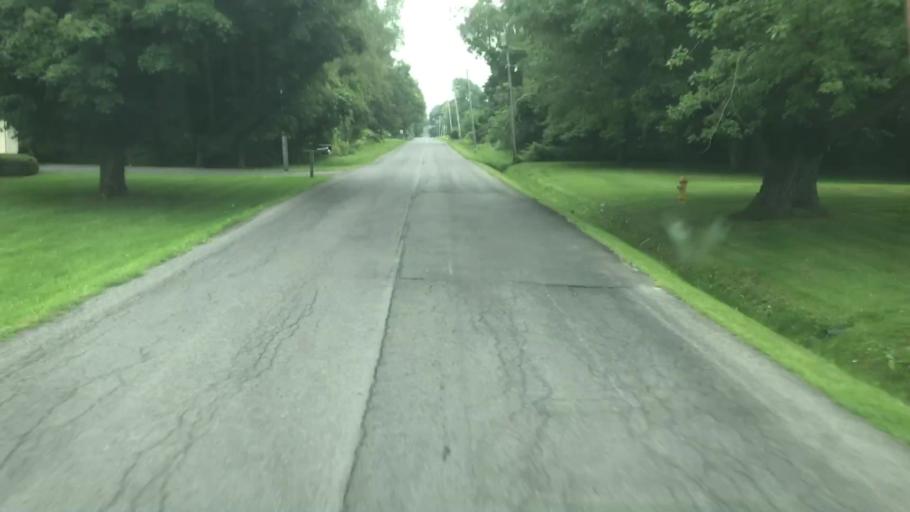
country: US
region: New York
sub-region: Onondaga County
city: Skaneateles
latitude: 42.9528
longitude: -76.4518
